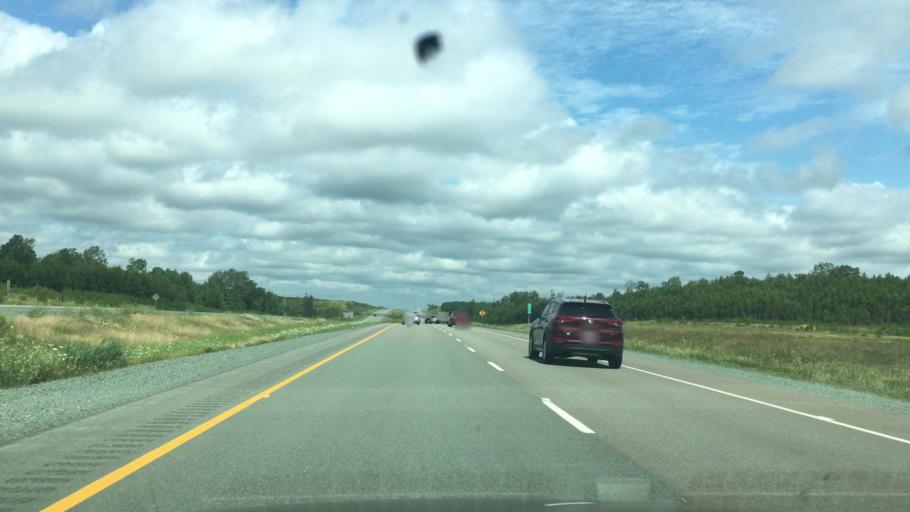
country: CA
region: Nova Scotia
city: Oxford
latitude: 45.6085
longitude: -63.7362
